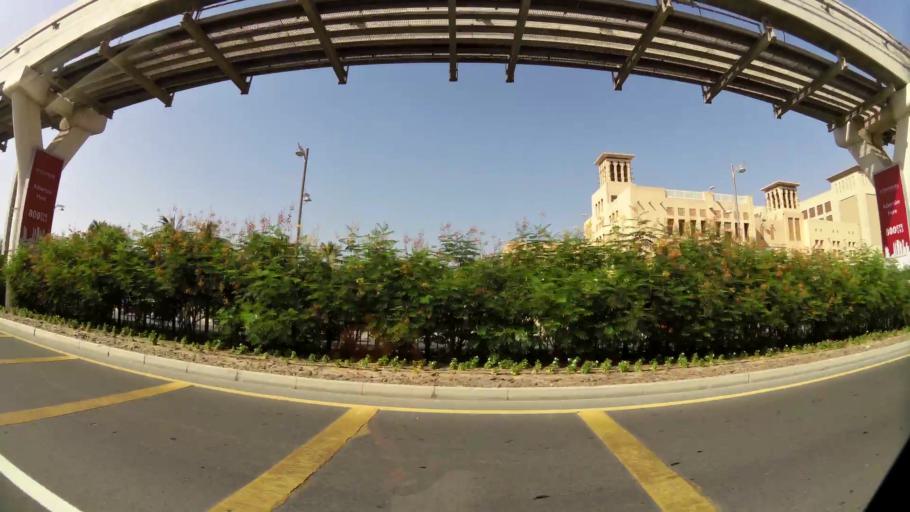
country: AE
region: Dubai
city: Dubai
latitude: 25.1172
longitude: 55.1351
